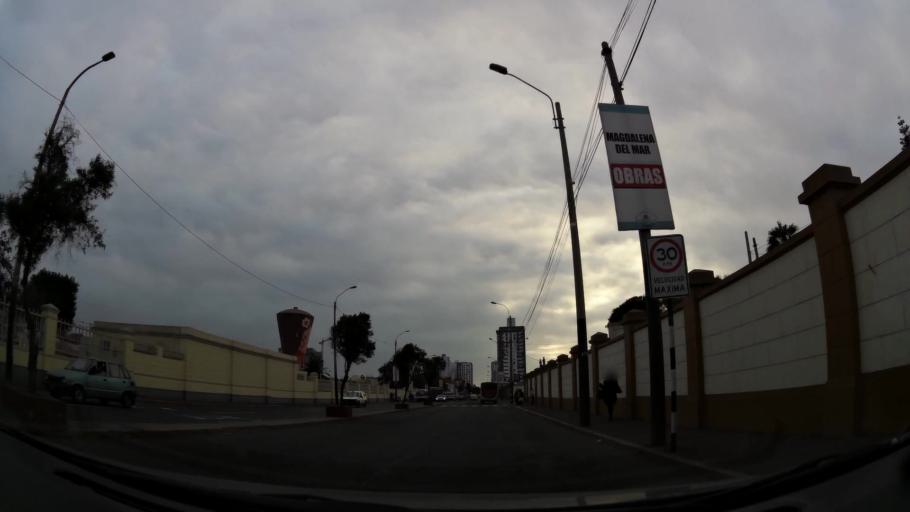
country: PE
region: Lima
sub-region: Lima
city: San Isidro
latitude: -12.0993
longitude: -77.0653
